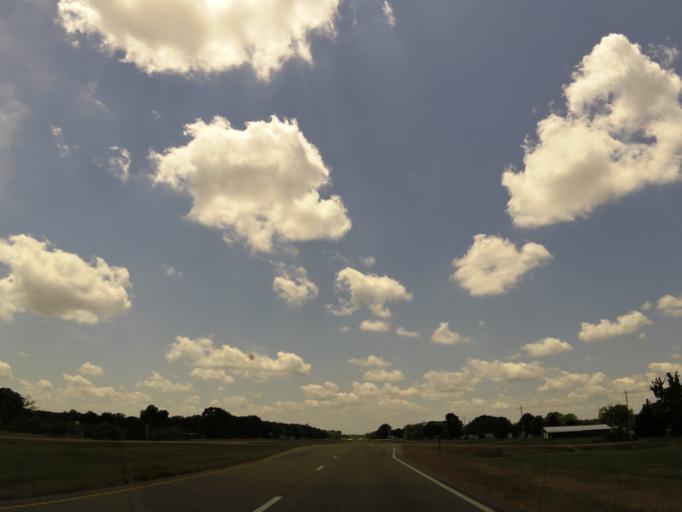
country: US
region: Mississippi
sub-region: Lee County
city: Verona
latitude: 34.2214
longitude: -88.8411
